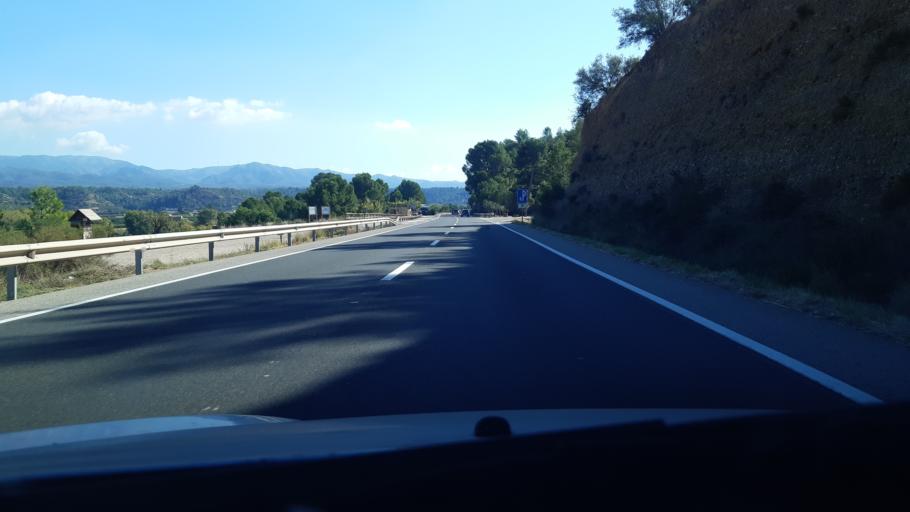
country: ES
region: Catalonia
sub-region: Provincia de Tarragona
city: Tivenys
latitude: 40.9223
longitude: 0.4900
